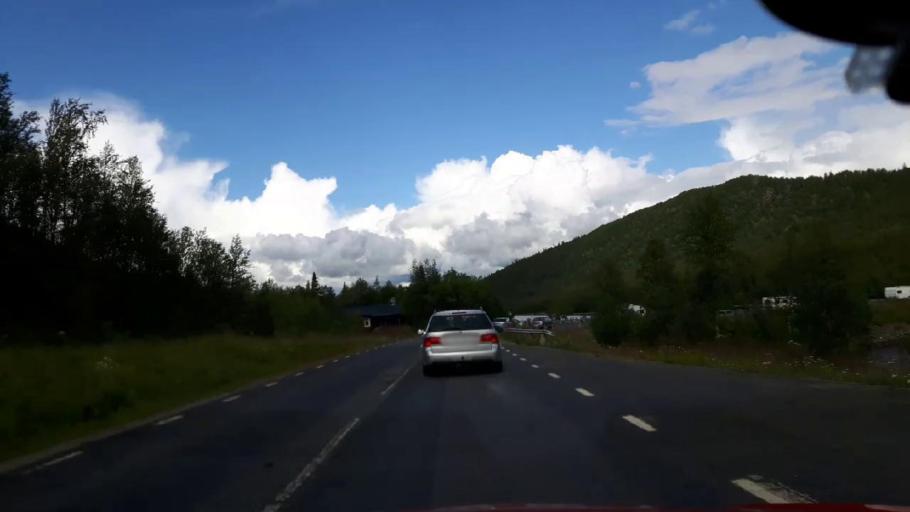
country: SE
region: Vaesterbotten
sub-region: Vilhelmina Kommun
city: Sjoberg
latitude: 65.0301
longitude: 15.1397
